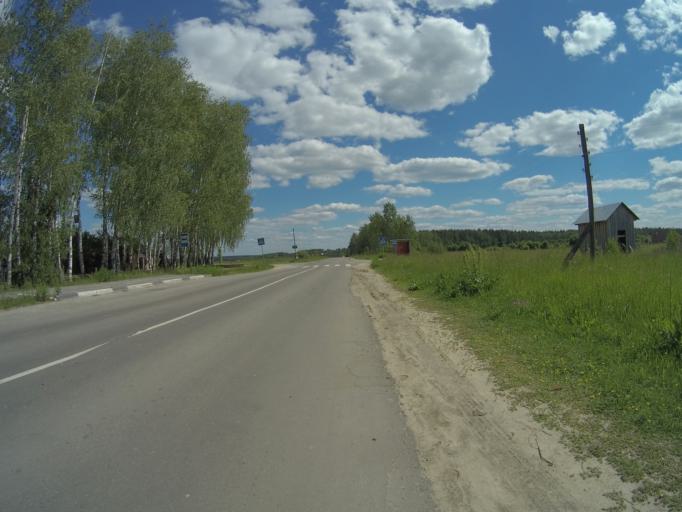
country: RU
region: Vladimir
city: Sudogda
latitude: 56.0683
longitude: 40.7988
